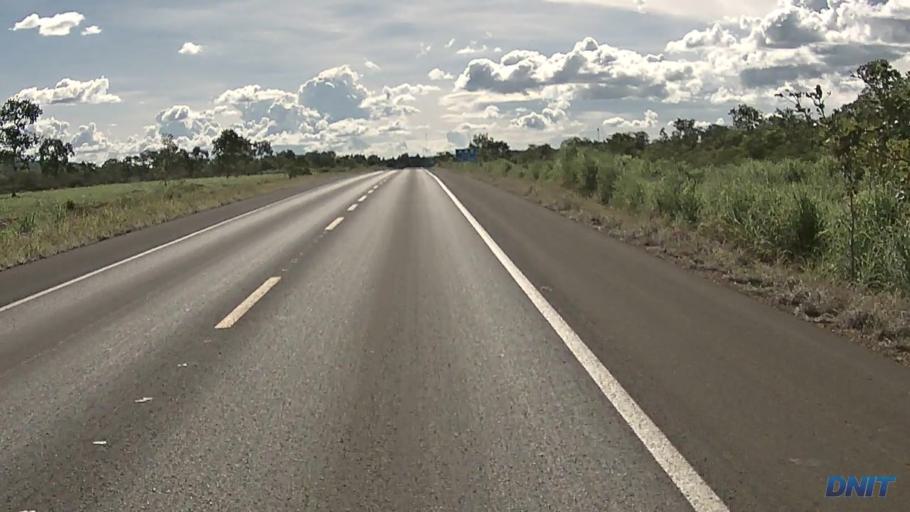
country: BR
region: Goias
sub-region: Barro Alto
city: Barro Alto
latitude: -15.2091
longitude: -48.6855
